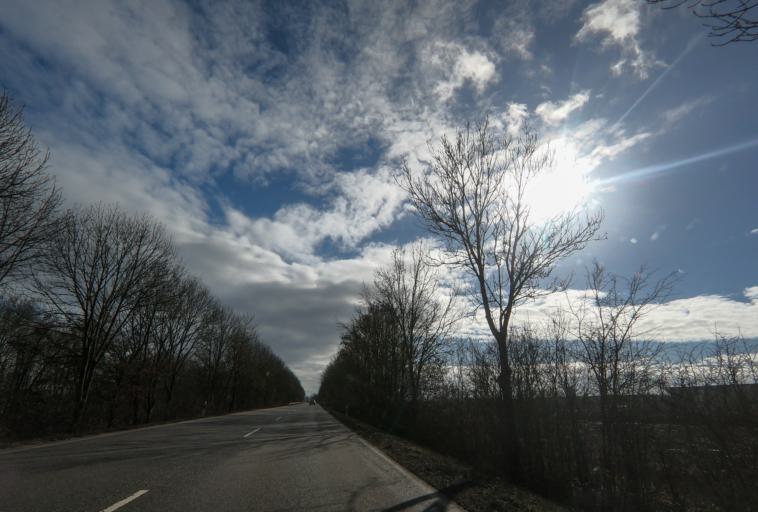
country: DE
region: Bavaria
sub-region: Upper Palatinate
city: Obertraubling
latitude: 48.9773
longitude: 12.1609
